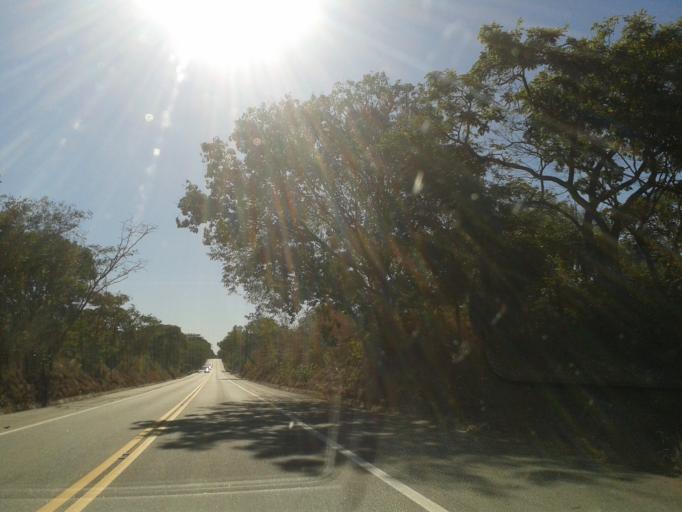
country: BR
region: Goias
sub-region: Itapuranga
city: Itapuranga
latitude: -15.4851
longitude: -50.3273
